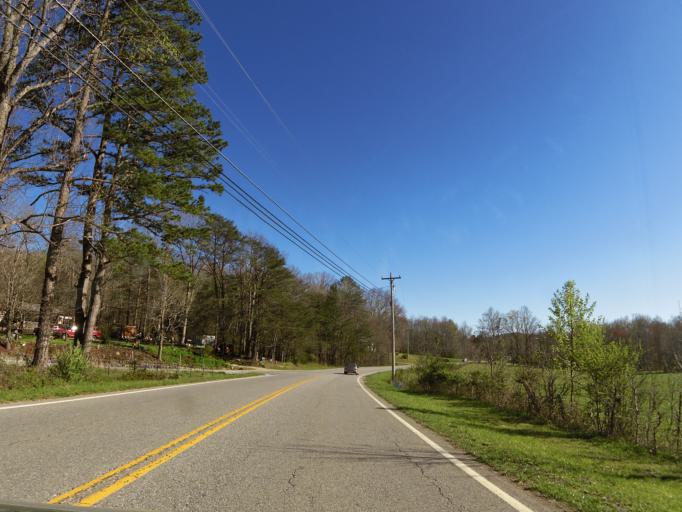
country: US
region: Tennessee
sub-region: Scott County
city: Huntsville
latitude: 36.4123
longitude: -84.4355
